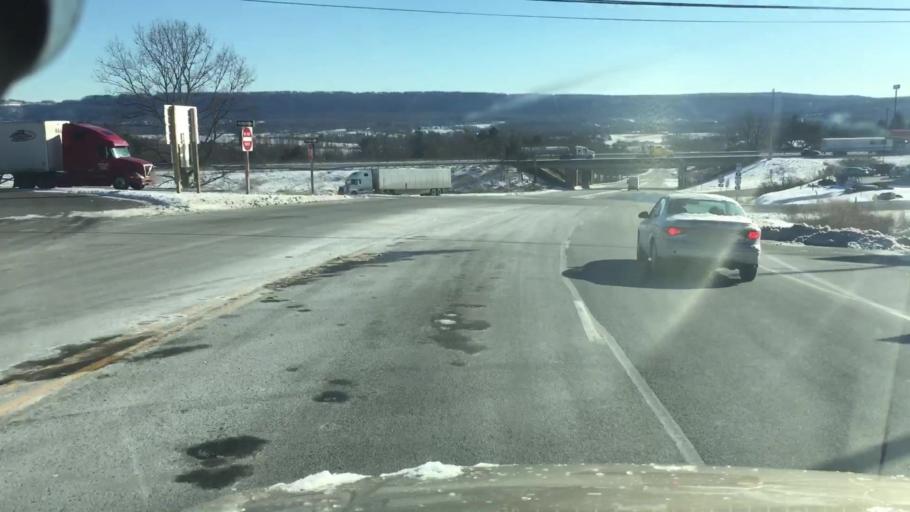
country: US
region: Pennsylvania
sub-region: Luzerne County
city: Conyngham
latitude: 41.0284
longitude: -76.0789
